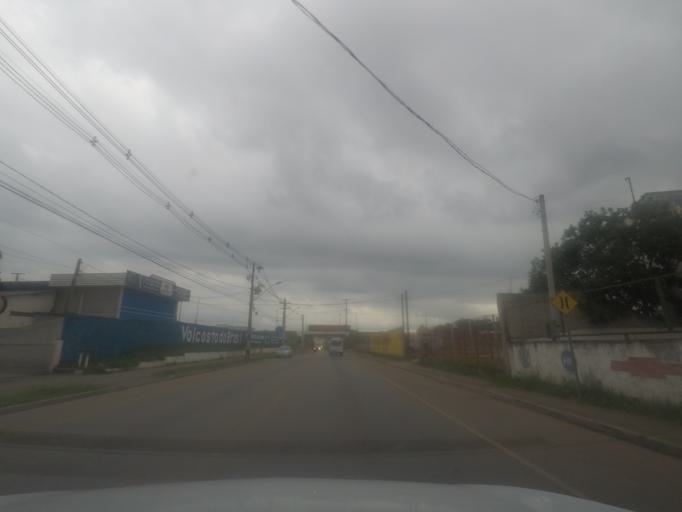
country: BR
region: Parana
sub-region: Sao Jose Dos Pinhais
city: Sao Jose dos Pinhais
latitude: -25.5598
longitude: -49.2627
